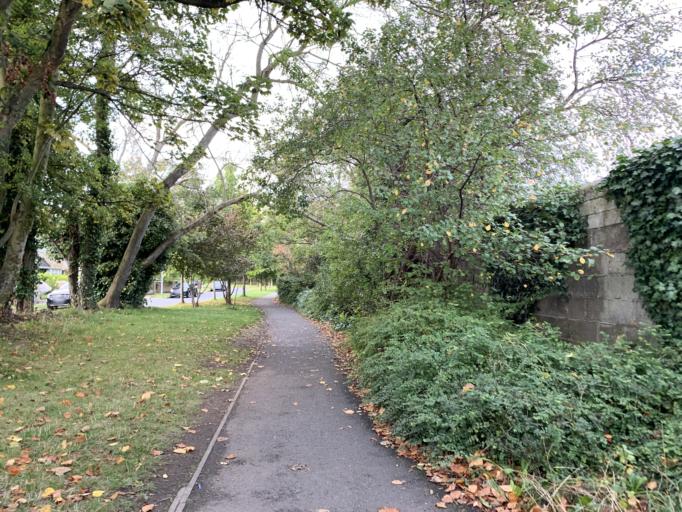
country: IE
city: Palmerstown
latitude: 53.3686
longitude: -6.3892
